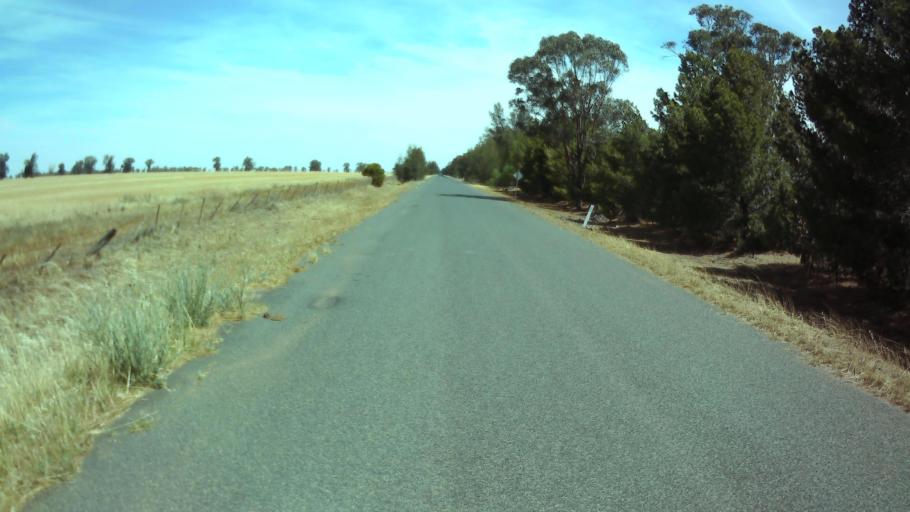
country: AU
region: New South Wales
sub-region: Weddin
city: Grenfell
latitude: -33.9150
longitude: 147.7652
